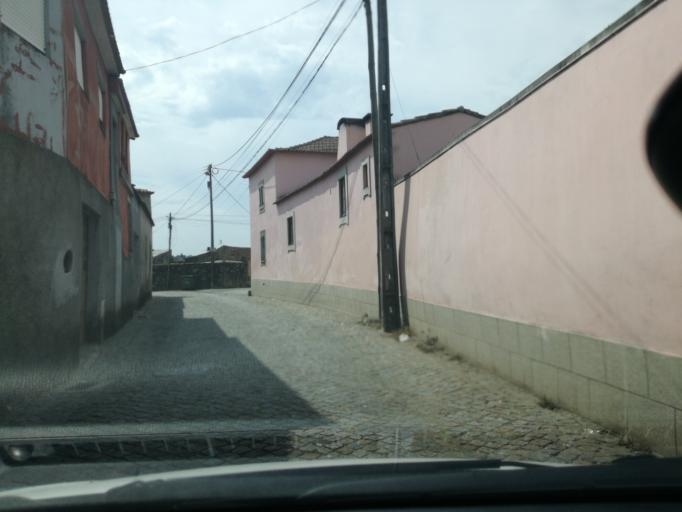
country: PT
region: Porto
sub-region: Vila Nova de Gaia
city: Grijo
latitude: 41.0239
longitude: -8.5890
